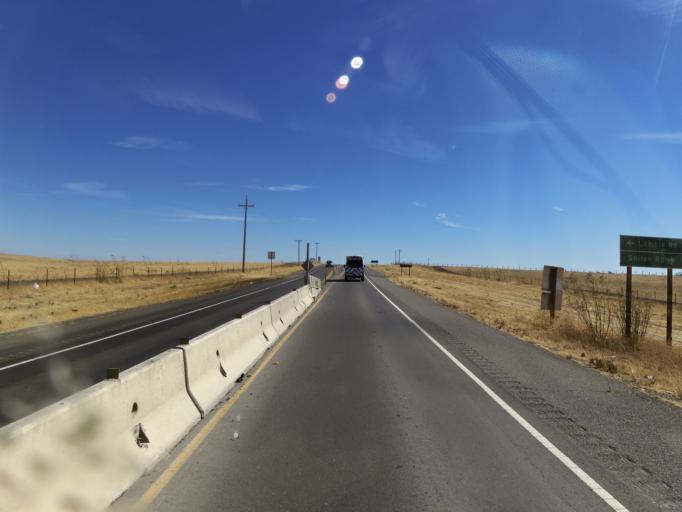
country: US
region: California
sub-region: Solano County
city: Suisun
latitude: 38.2223
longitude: -121.8907
